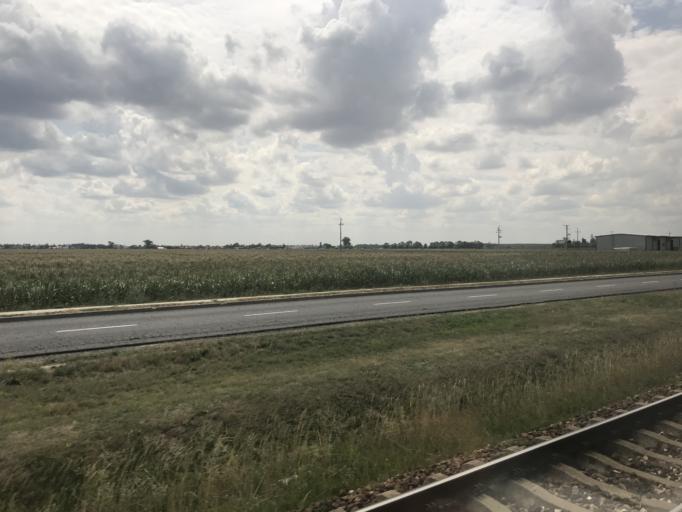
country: PL
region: Greater Poland Voivodeship
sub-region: Powiat poznanski
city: Dopiewo
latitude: 52.3581
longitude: 16.6898
